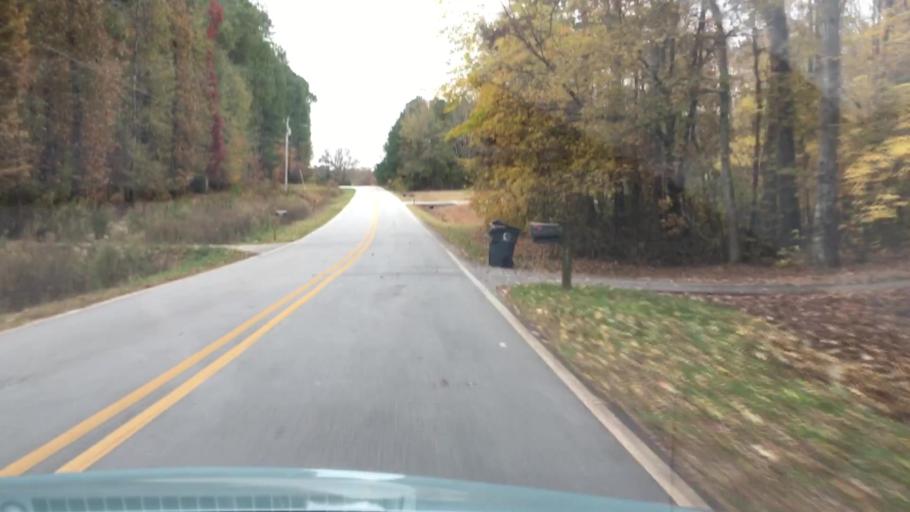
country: US
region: Georgia
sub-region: Henry County
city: McDonough
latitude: 33.5178
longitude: -84.1287
